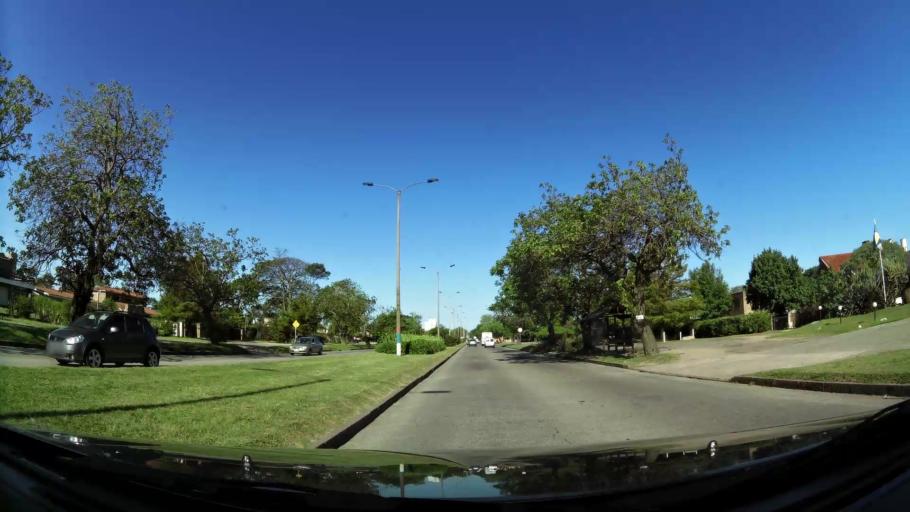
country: UY
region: Canelones
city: Paso de Carrasco
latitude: -34.8777
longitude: -56.0625
